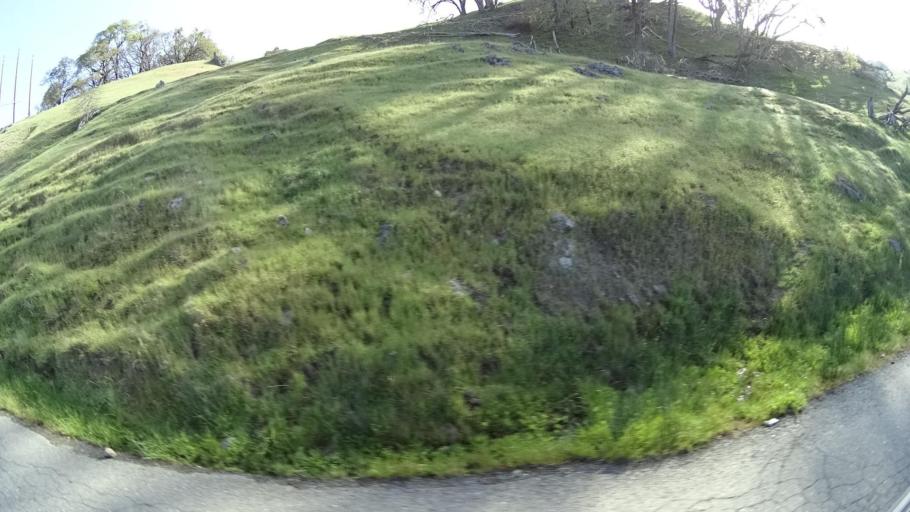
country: US
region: California
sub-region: Humboldt County
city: Blue Lake
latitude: 40.7106
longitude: -123.9400
